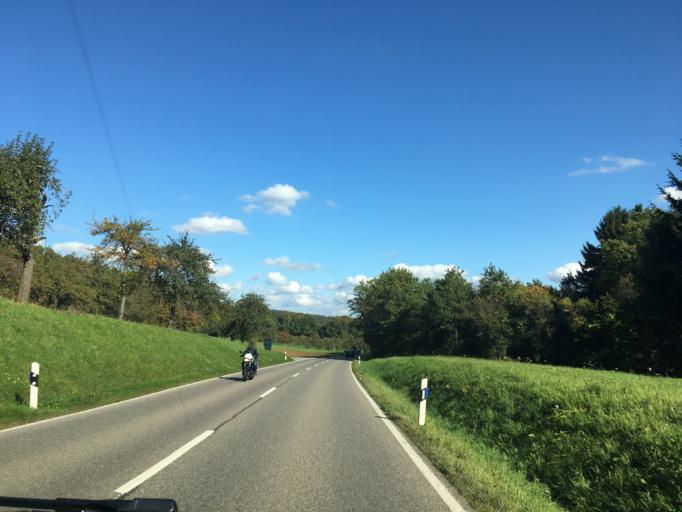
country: DE
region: Baden-Wuerttemberg
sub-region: Karlsruhe Region
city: Althengstett
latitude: 48.7281
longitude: 8.8154
